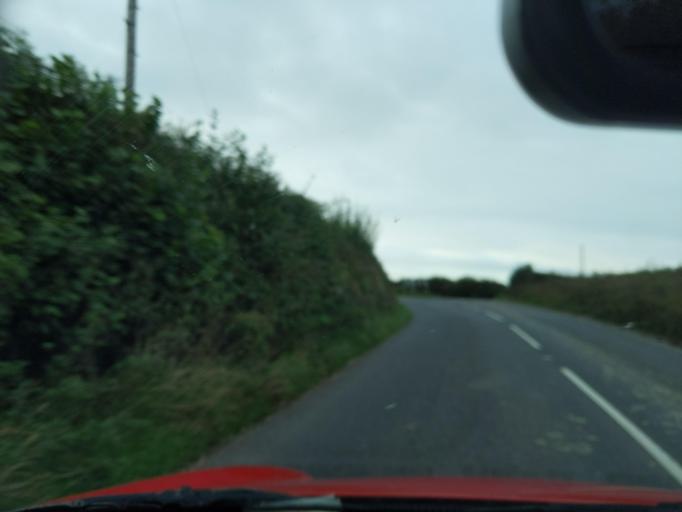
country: GB
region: England
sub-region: Devon
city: Great Torrington
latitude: 50.9118
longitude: -4.1234
